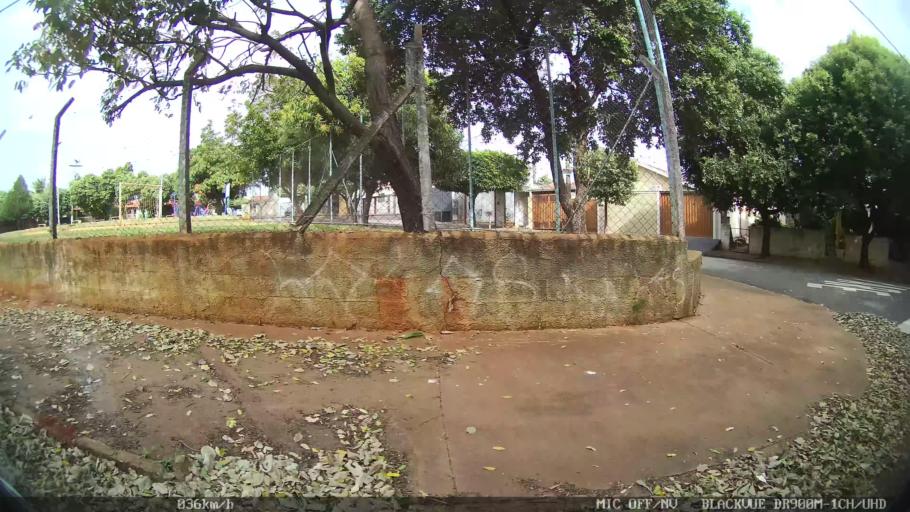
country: BR
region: Sao Paulo
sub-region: Sao Jose Do Rio Preto
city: Sao Jose do Rio Preto
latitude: -20.8130
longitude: -49.3544
